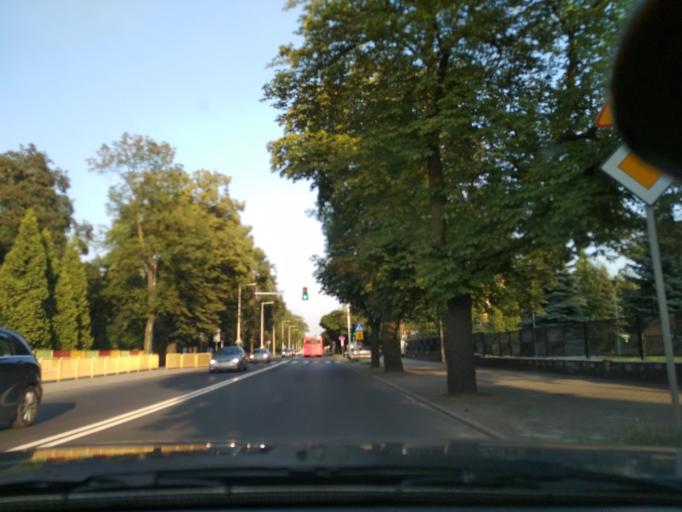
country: PL
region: Silesian Voivodeship
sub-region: Powiat zawiercianski
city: Zawiercie
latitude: 50.4804
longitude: 19.4409
